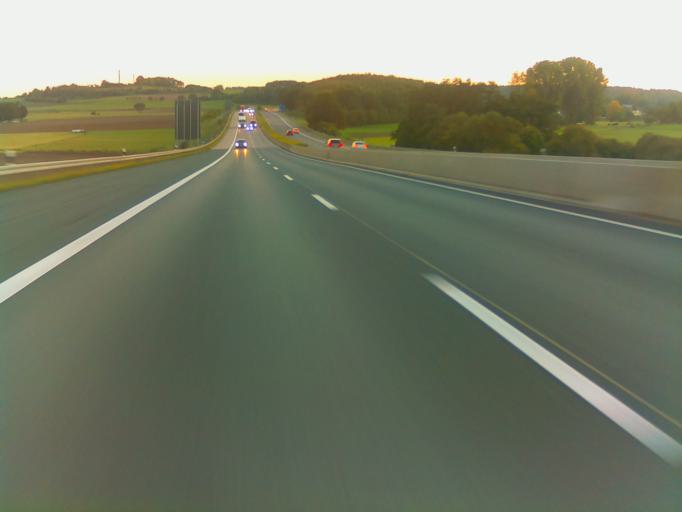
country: DE
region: Hesse
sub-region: Regierungsbezirk Giessen
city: Reiskirchen
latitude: 50.5934
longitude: 8.8127
